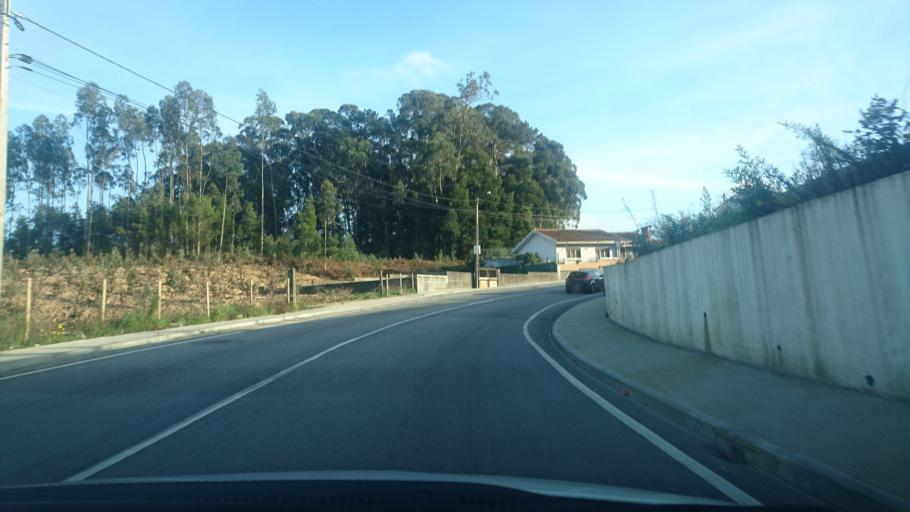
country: PT
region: Aveiro
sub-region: Espinho
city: Souto
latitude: 40.9731
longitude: -8.6080
